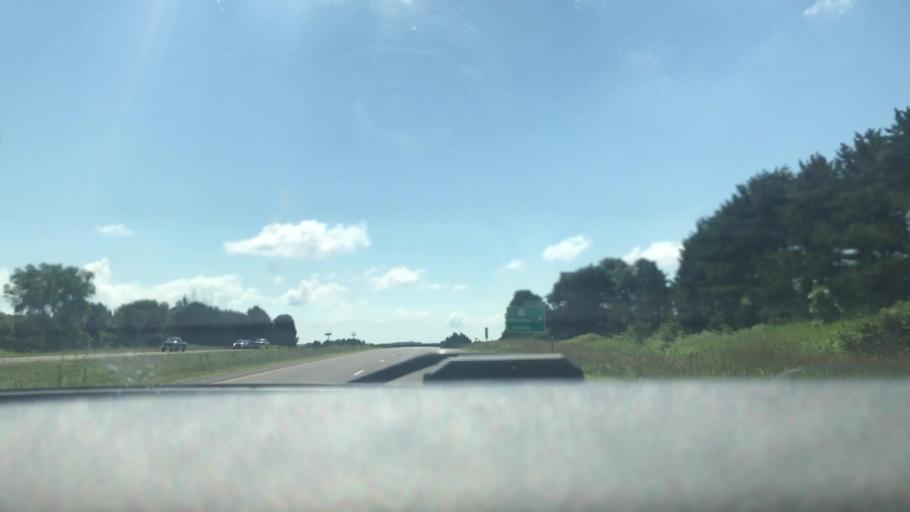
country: US
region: Wisconsin
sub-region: Chippewa County
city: Bloomer
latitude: 45.1042
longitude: -91.5113
